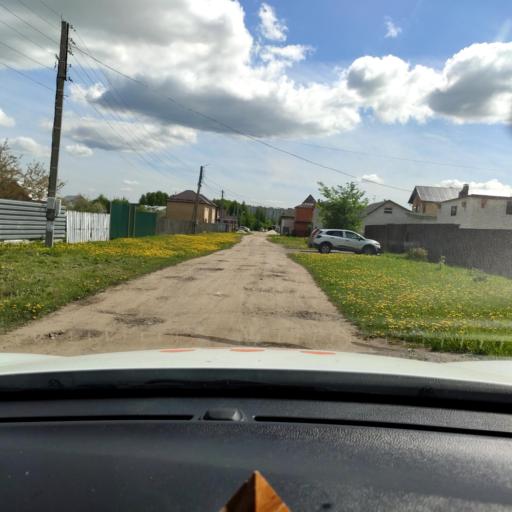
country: RU
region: Tatarstan
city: Osinovo
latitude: 55.8798
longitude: 48.8689
